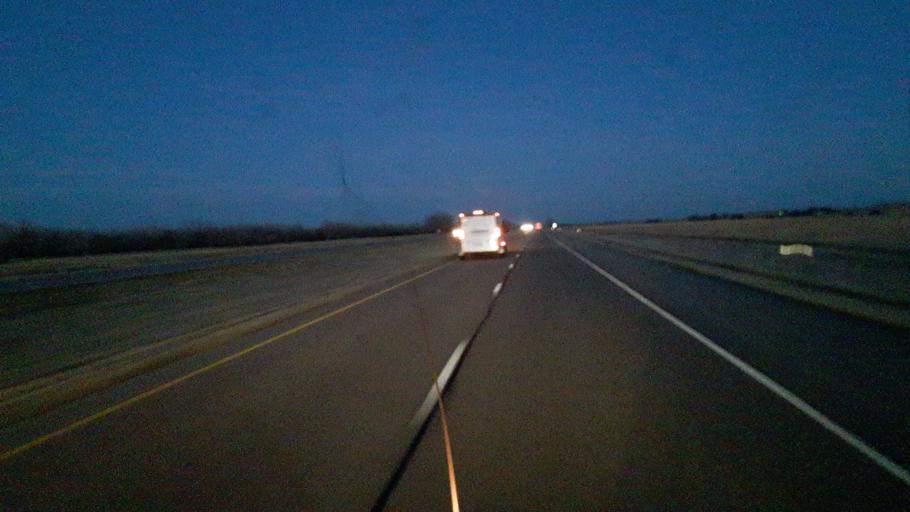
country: US
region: Nebraska
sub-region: Lincoln County
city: Sutherland
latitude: 41.1146
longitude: -101.3154
